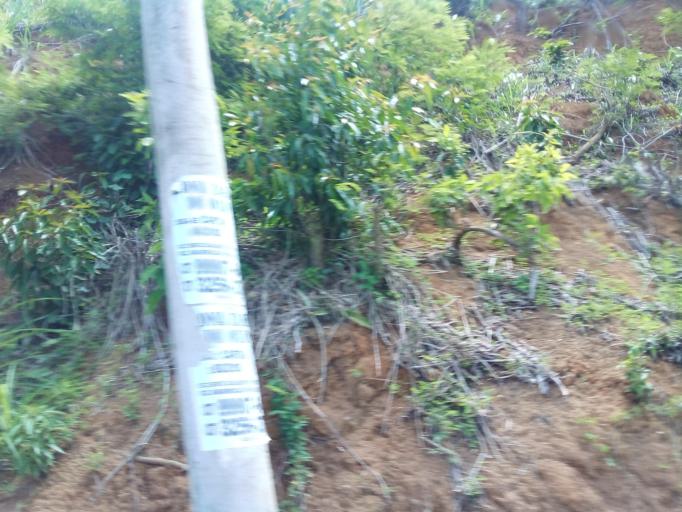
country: BR
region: Espirito Santo
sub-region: Ibiracu
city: Ibiracu
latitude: -19.8420
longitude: -40.3539
